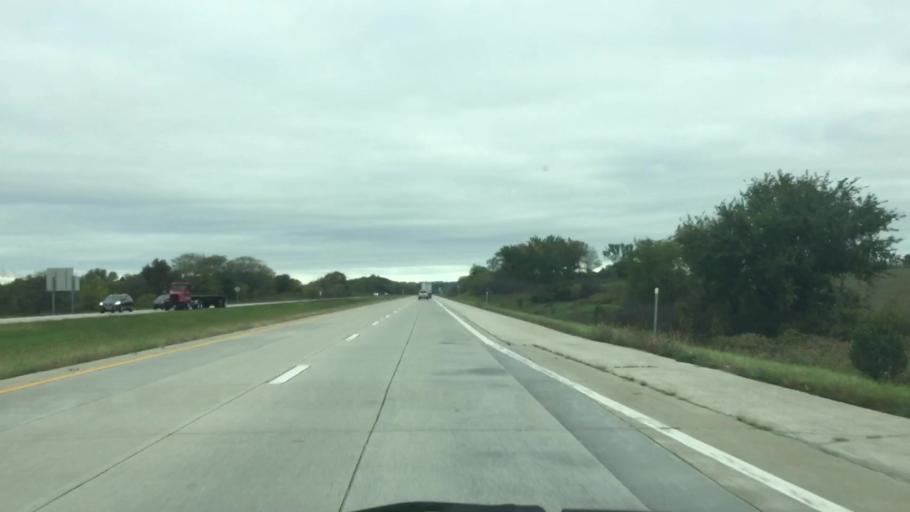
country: US
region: Missouri
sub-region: Daviess County
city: Gallatin
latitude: 40.0009
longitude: -94.0958
